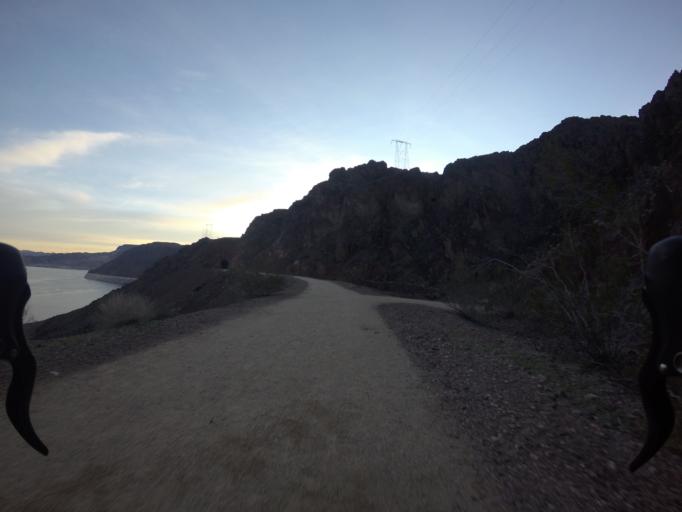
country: US
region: Nevada
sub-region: Clark County
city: Boulder City
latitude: 36.0161
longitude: -114.7652
